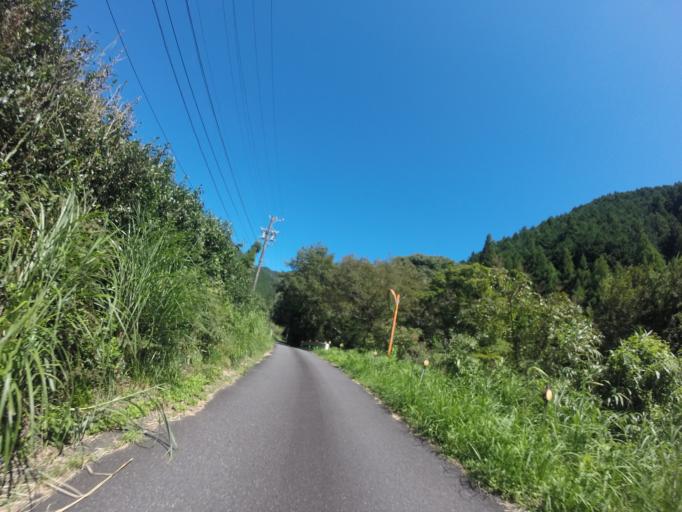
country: JP
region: Shizuoka
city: Fujieda
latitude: 34.9551
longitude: 138.1674
